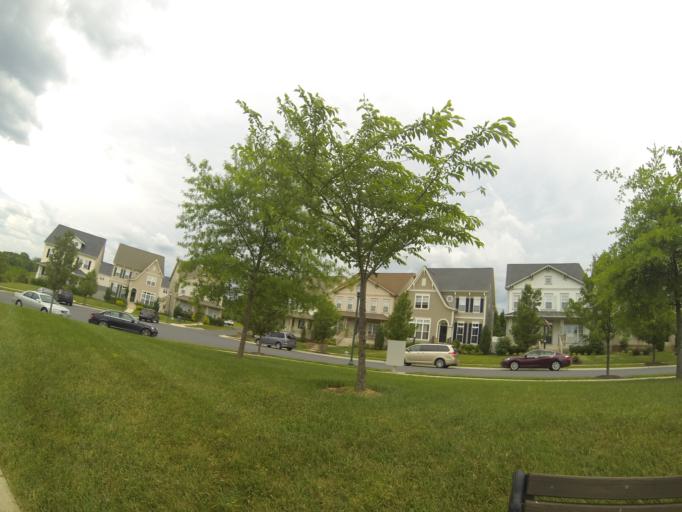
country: US
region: Maryland
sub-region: Montgomery County
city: Clarksburg
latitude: 39.2456
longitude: -77.2864
